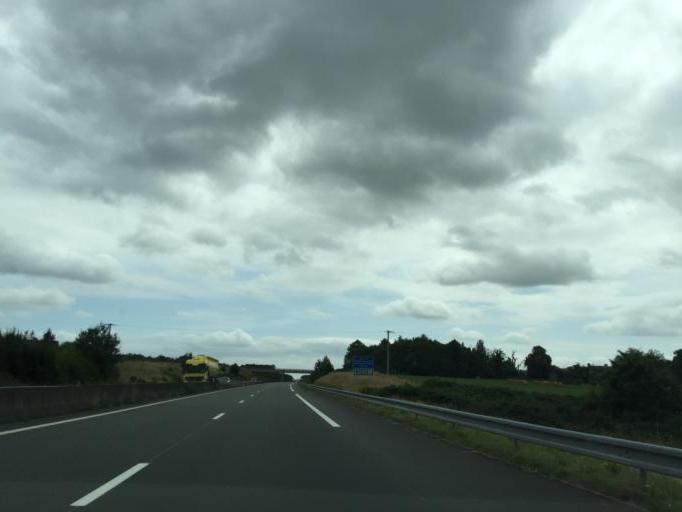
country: FR
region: Pays de la Loire
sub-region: Departement de la Sarthe
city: Mayet
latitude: 47.7710
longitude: 0.3139
